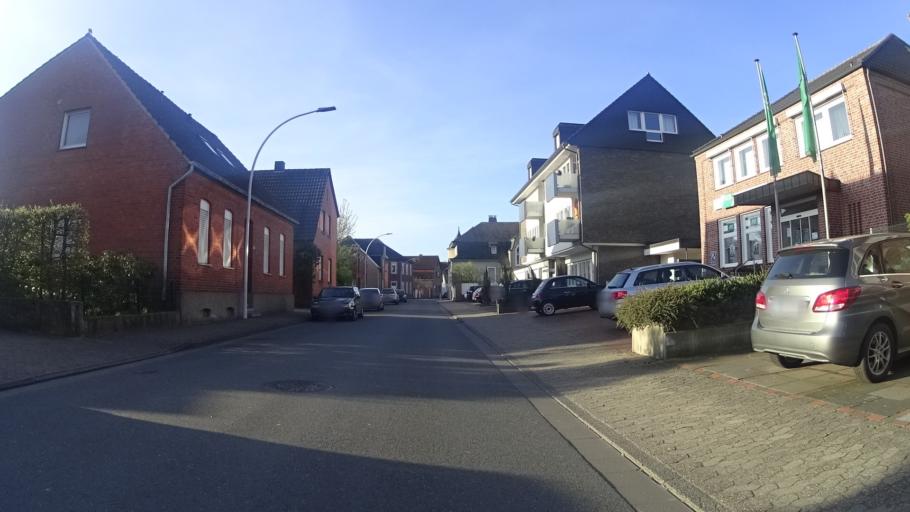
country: DE
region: North Rhine-Westphalia
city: Emsdetten
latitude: 52.1777
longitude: 7.5234
